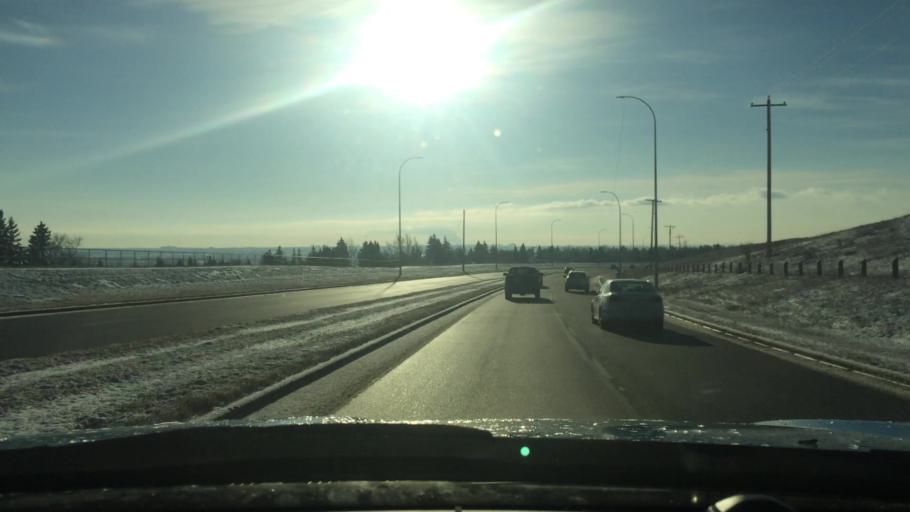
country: CA
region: Alberta
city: Calgary
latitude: 51.1173
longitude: -114.0866
